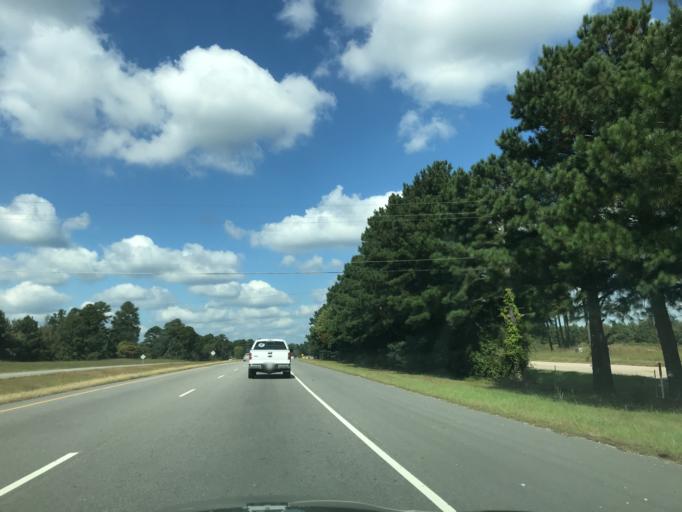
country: US
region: North Carolina
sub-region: Wake County
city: Wake Forest
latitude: 35.9325
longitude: -78.5430
